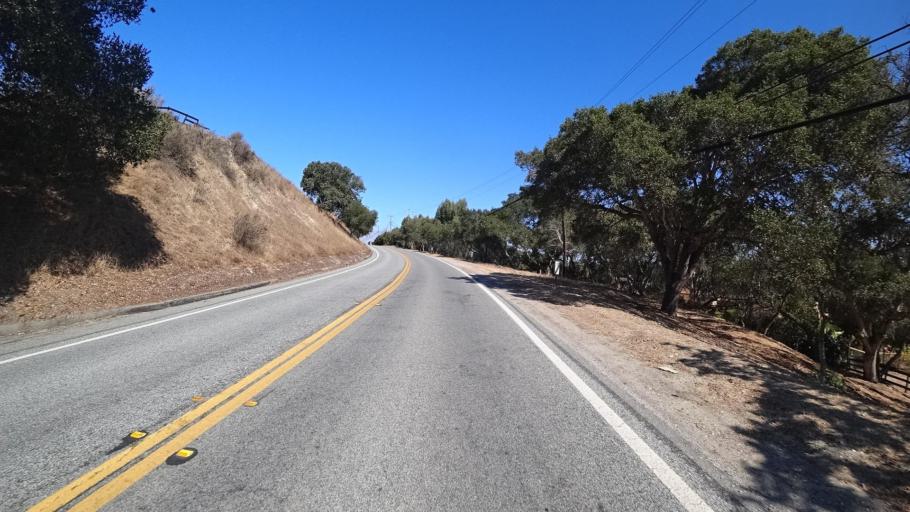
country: US
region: California
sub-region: Monterey County
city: Carmel Valley Village
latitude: 36.5595
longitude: -121.7330
